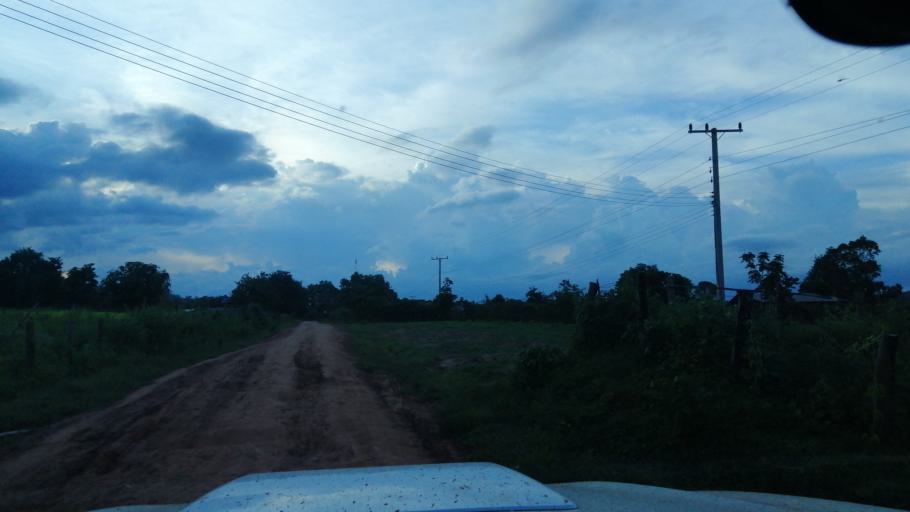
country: TH
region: Uttaradit
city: Ban Khok
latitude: 17.8674
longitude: 101.0956
